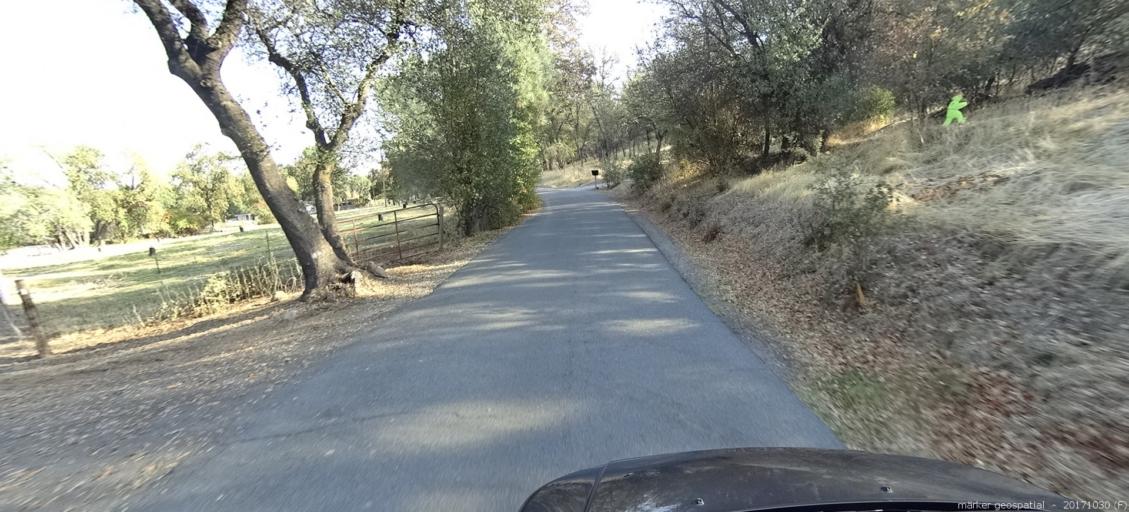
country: US
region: California
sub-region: Shasta County
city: Palo Cedro
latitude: 40.5553
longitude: -122.1628
